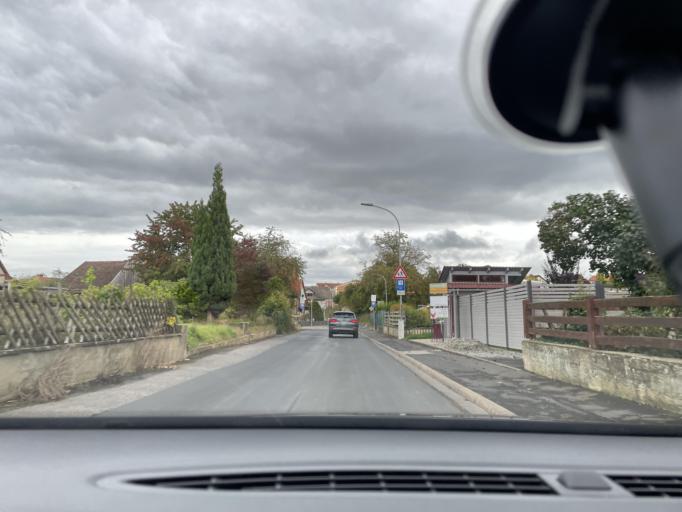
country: DE
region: Bavaria
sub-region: Regierungsbezirk Unterfranken
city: Rodelmaier
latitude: 50.3197
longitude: 10.2762
